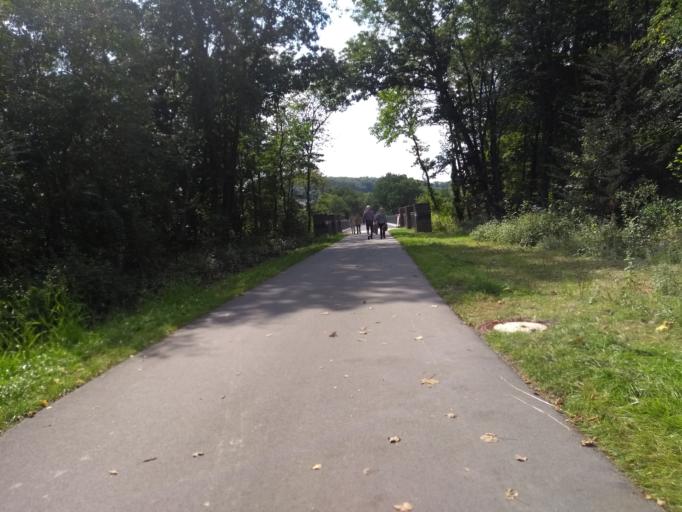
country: DE
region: North Rhine-Westphalia
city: Witten
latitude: 51.4012
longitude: 7.3391
